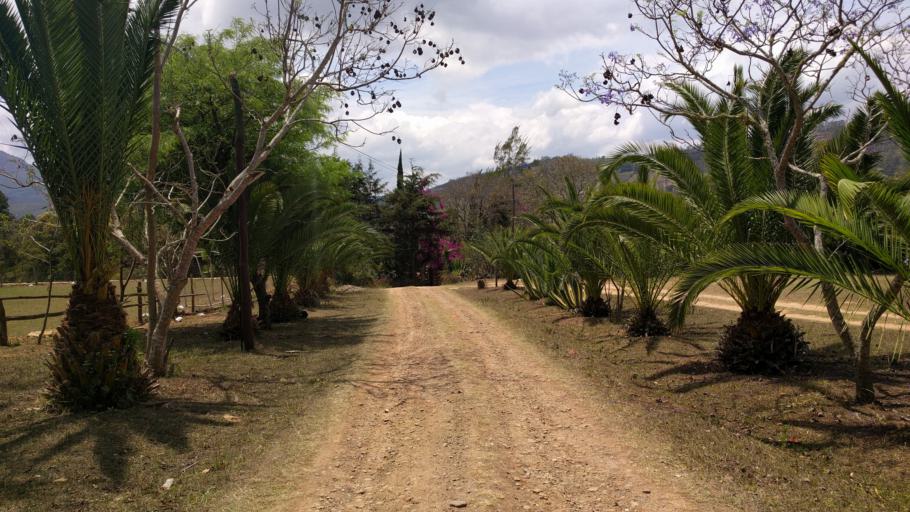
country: BO
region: Santa Cruz
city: Samaipata
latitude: -18.1881
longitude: -63.8799
